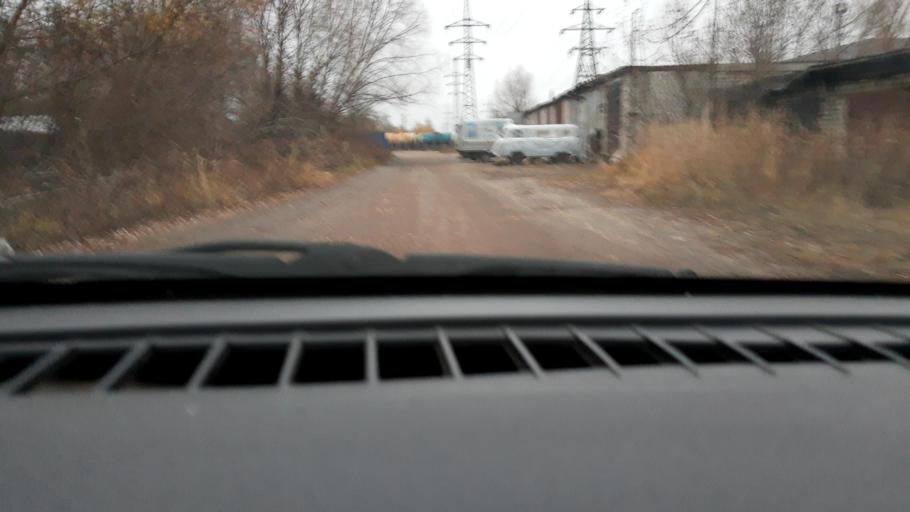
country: RU
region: Nizjnij Novgorod
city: Nizhniy Novgorod
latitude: 56.3066
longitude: 43.8793
